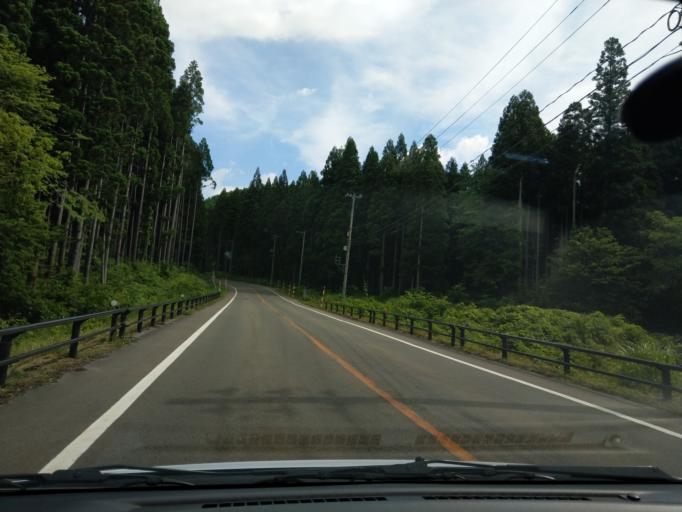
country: JP
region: Akita
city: Kakunodatemachi
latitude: 39.7099
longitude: 140.5873
